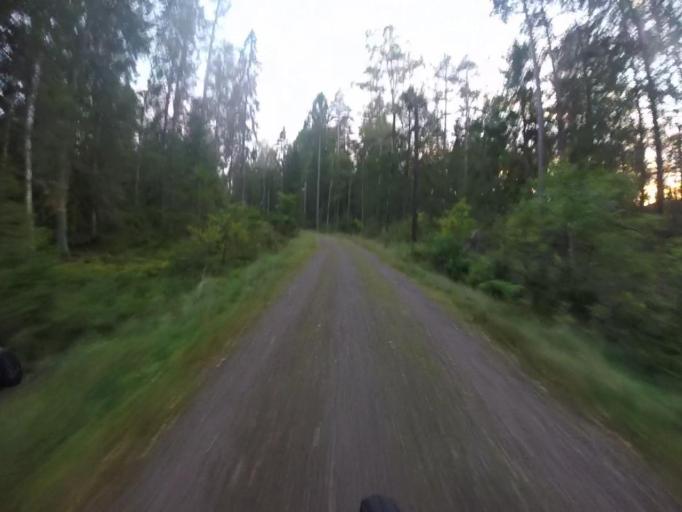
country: SE
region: Vaestra Goetaland
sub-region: Trollhattan
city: Trollhattan
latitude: 58.2966
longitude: 12.2536
